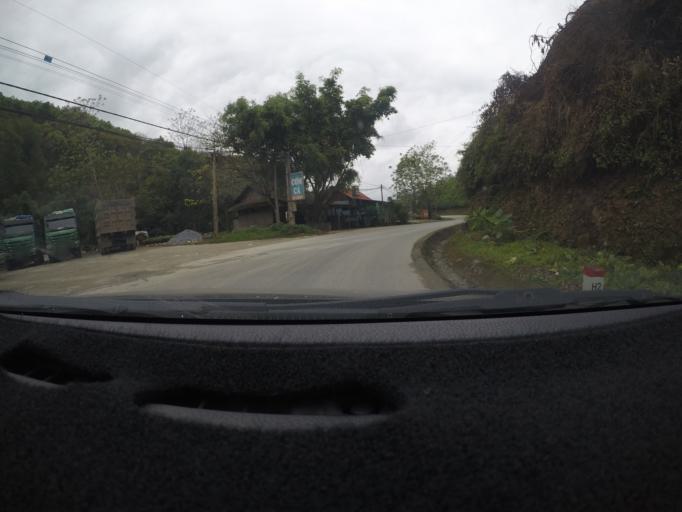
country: VN
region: Yen Bai
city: Thi Tran Yen The
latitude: 21.9328
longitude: 104.7890
